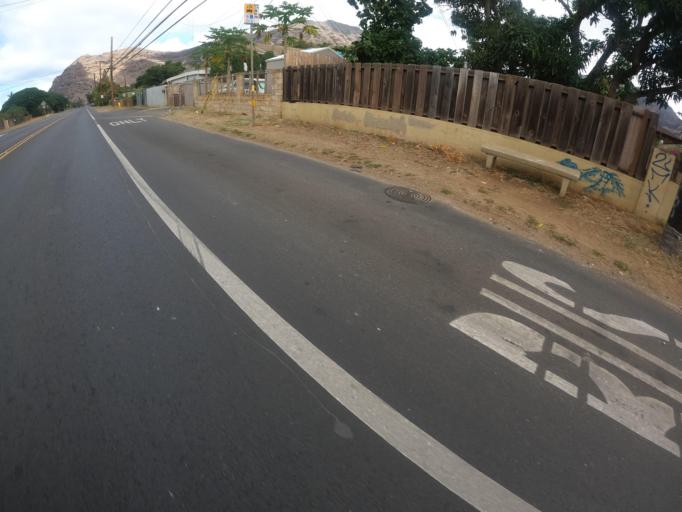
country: US
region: Hawaii
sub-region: Honolulu County
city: Makaha
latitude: 21.4643
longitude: -158.2130
